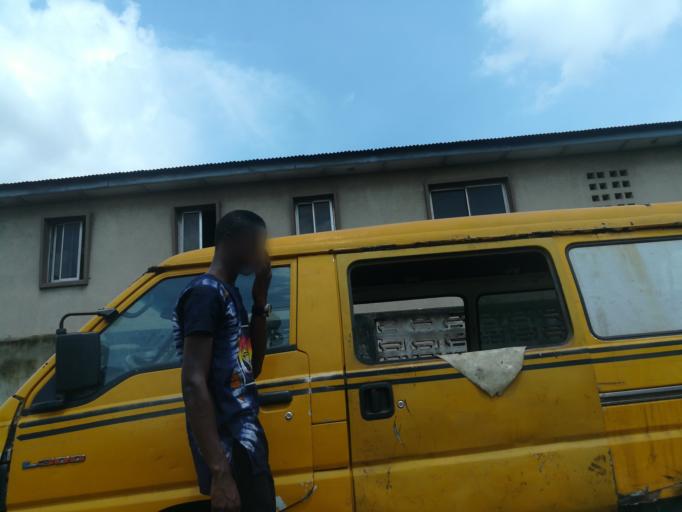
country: NG
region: Lagos
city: Somolu
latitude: 6.5391
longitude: 3.3654
